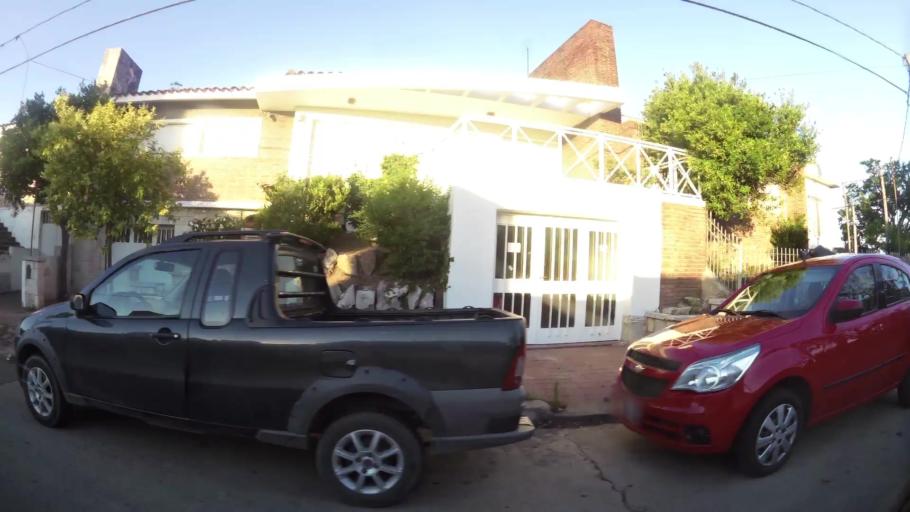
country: AR
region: Cordoba
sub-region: Departamento de Capital
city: Cordoba
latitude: -31.3835
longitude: -64.2093
